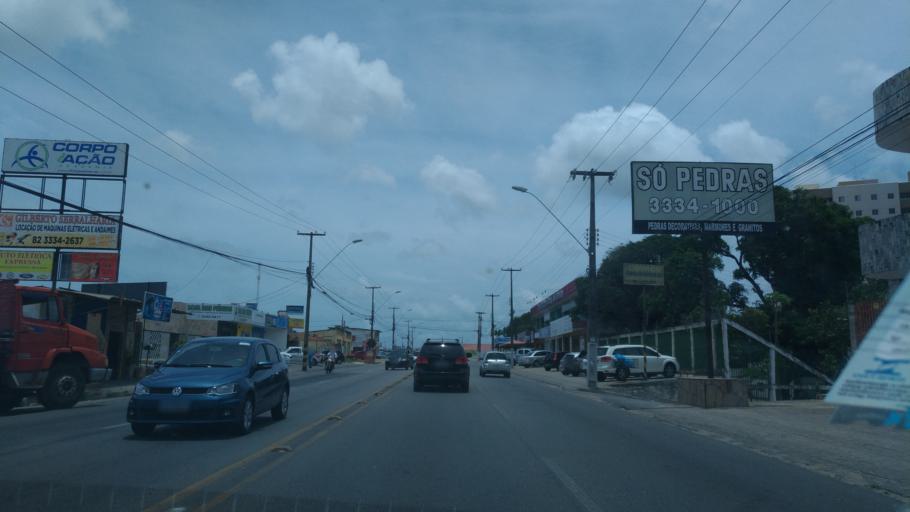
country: BR
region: Alagoas
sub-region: Satuba
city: Satuba
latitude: -9.5666
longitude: -35.7440
